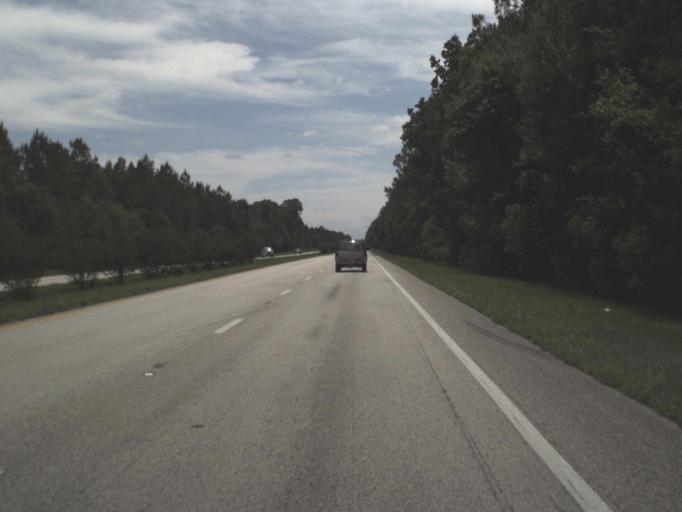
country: US
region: Florida
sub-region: Nassau County
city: Nassau Village-Ratliff
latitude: 30.4725
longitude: -81.7798
